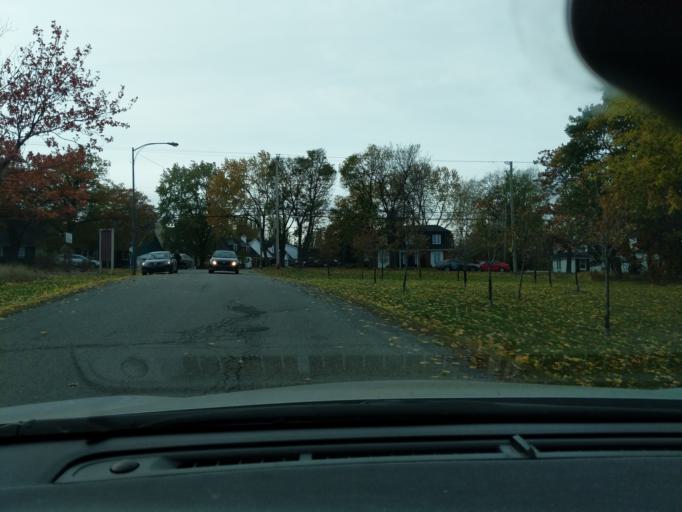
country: CA
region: Quebec
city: Quebec
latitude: 46.7759
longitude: -71.2526
